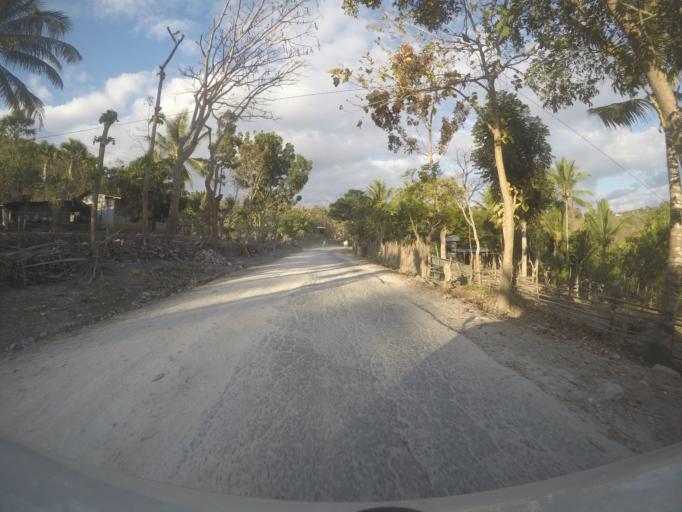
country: TL
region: Bobonaro
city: Maliana
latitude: -8.9624
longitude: 125.0319
